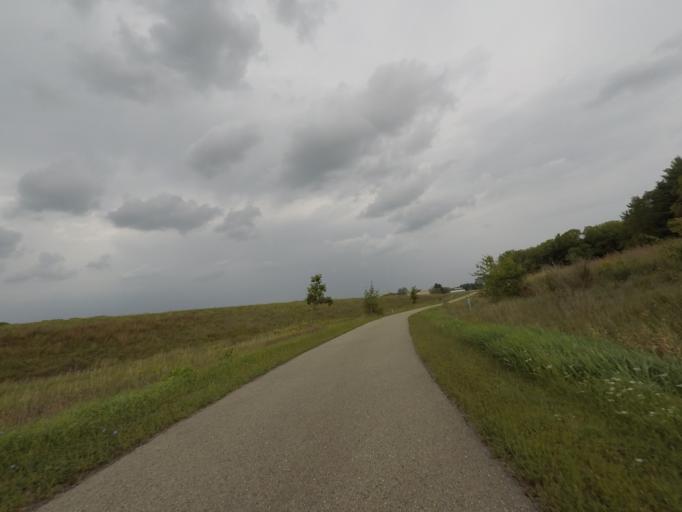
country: US
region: Wisconsin
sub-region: Jefferson County
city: Jefferson
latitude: 42.9854
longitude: -88.8292
